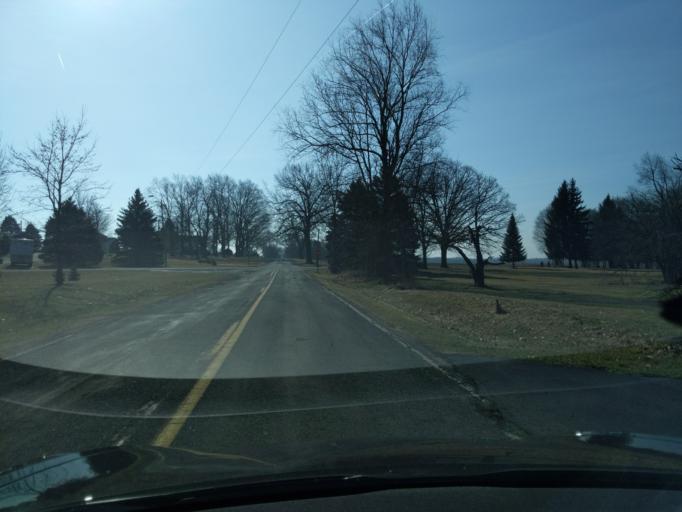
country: US
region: Michigan
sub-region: Ingham County
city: Leslie
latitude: 42.3761
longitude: -84.4440
